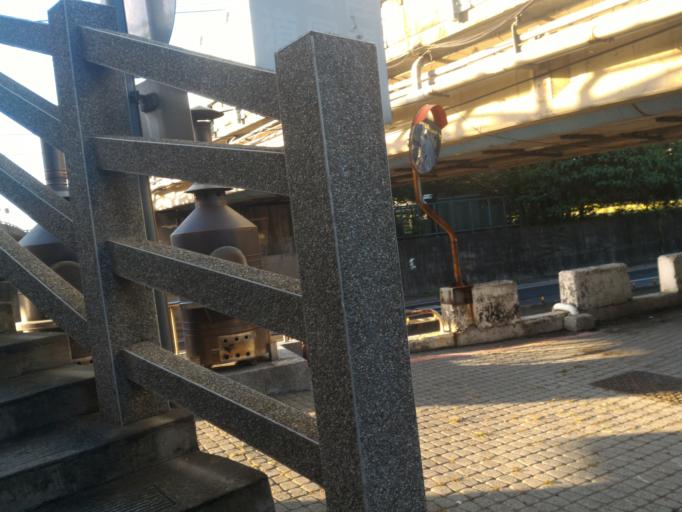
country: TW
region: Taiwan
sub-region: Taoyuan
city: Taoyuan
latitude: 24.9688
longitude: 121.3938
